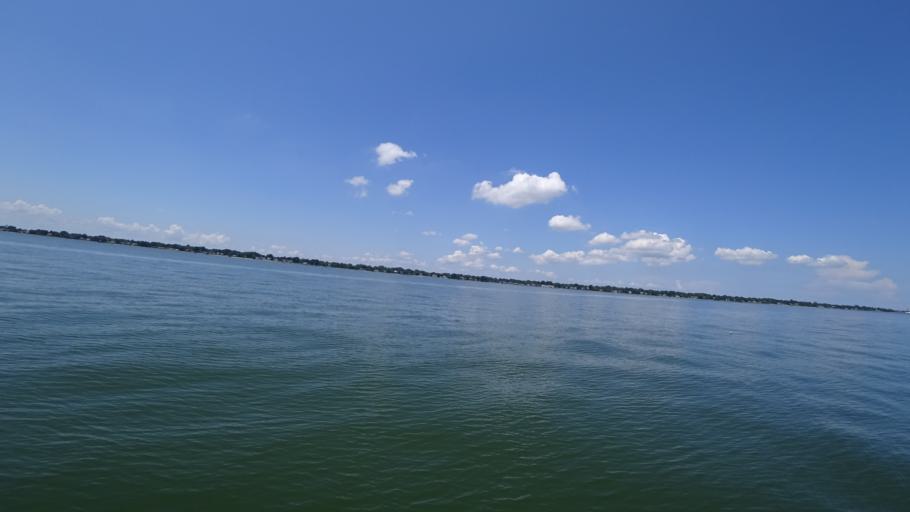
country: US
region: Virginia
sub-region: City of Hampton
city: Hampton
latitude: 36.9851
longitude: -76.3688
